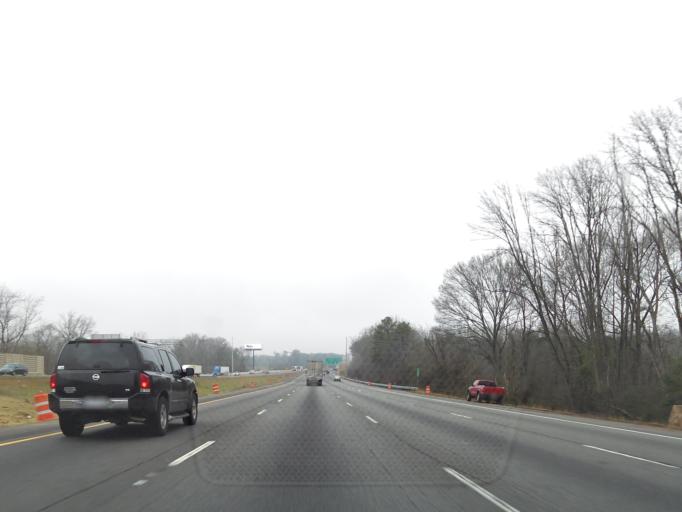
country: US
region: Georgia
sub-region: Henry County
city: Stockbridge
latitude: 33.5134
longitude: -84.2397
